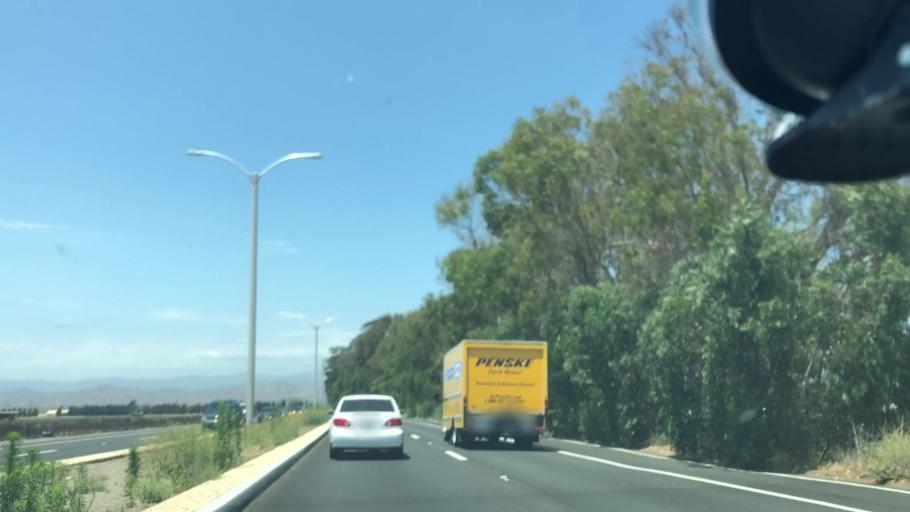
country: US
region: California
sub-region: Ventura County
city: Oxnard Shores
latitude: 34.2122
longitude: -119.2209
